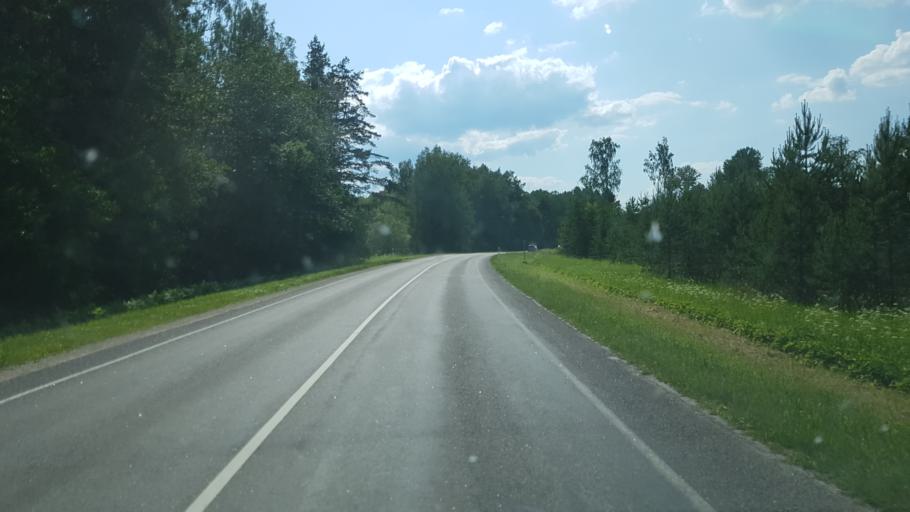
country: EE
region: Jogevamaa
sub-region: Jogeva linn
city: Jogeva
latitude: 58.7376
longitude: 26.2953
